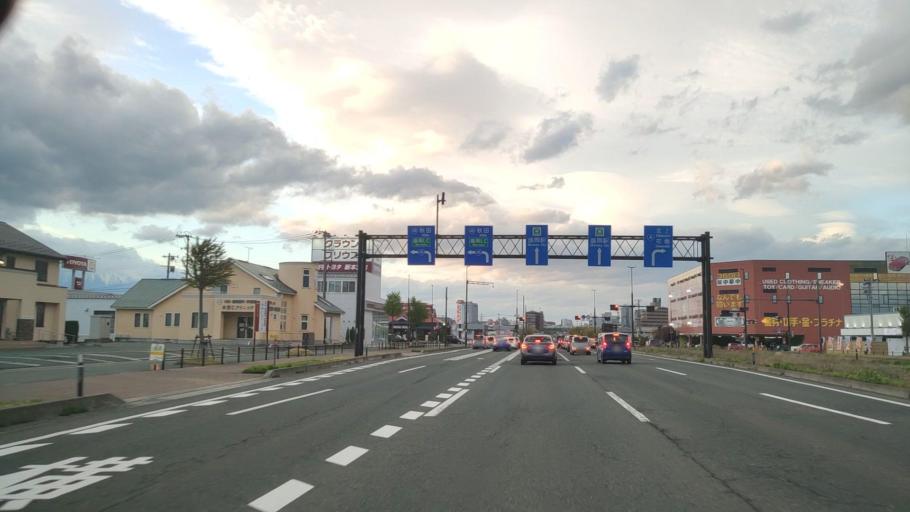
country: JP
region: Iwate
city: Morioka-shi
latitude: 39.6836
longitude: 141.1354
